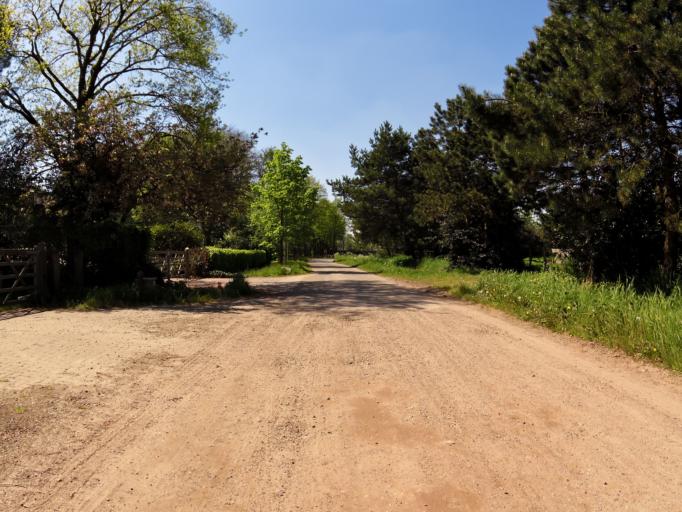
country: NL
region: North Brabant
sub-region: Gemeente Haaren
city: Haaren
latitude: 51.6529
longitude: 5.2203
